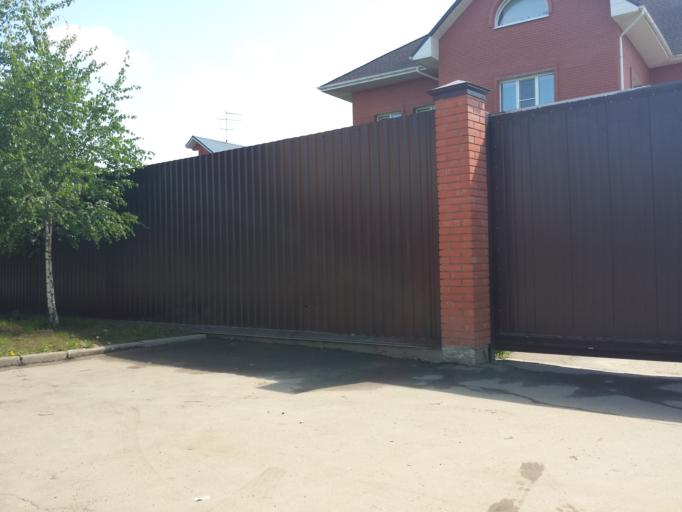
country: RU
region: Moskovskaya
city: Povedniki
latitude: 55.9301
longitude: 37.6152
